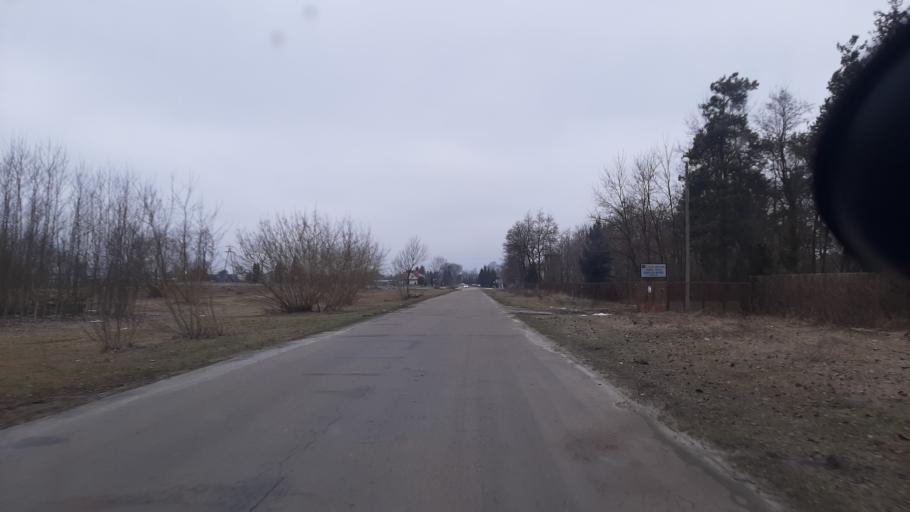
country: PL
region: Lublin Voivodeship
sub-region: Powiat wlodawski
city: Wlodawa
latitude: 51.5208
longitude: 23.5837
